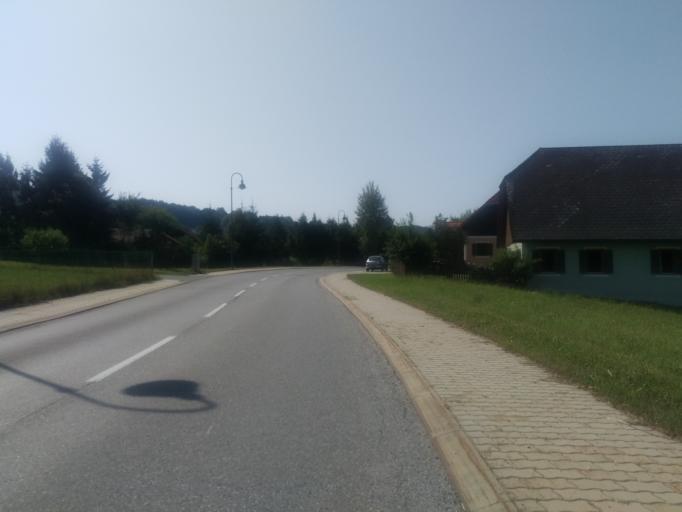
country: AT
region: Styria
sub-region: Politischer Bezirk Graz-Umgebung
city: Fernitz
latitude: 46.9653
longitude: 15.5048
